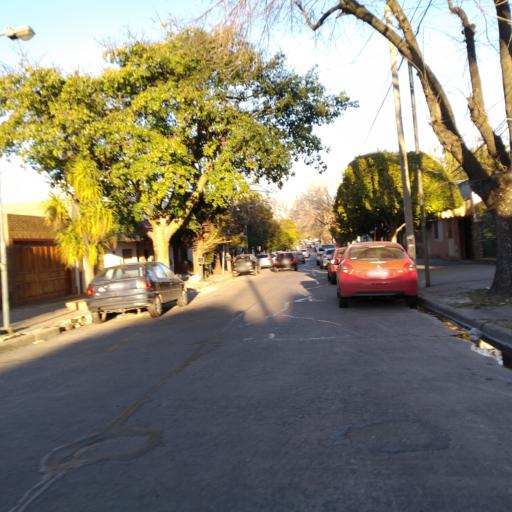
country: AR
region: Buenos Aires
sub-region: Partido de La Plata
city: La Plata
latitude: -34.9344
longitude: -57.9738
